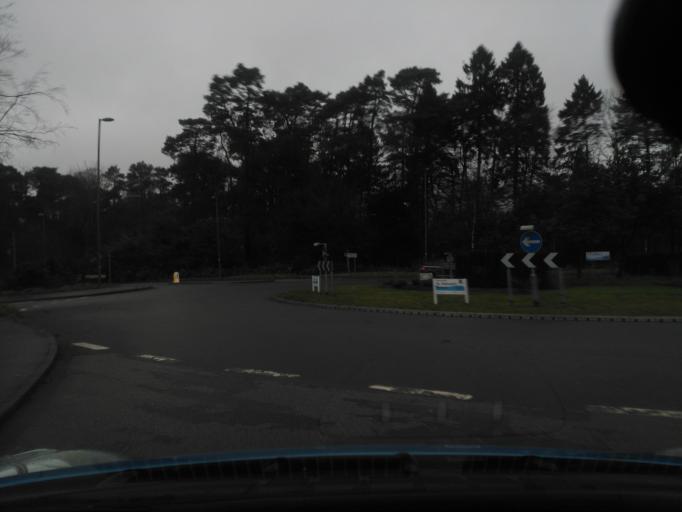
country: GB
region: England
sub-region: Surrey
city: Hindhead
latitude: 51.1065
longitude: -0.7429
